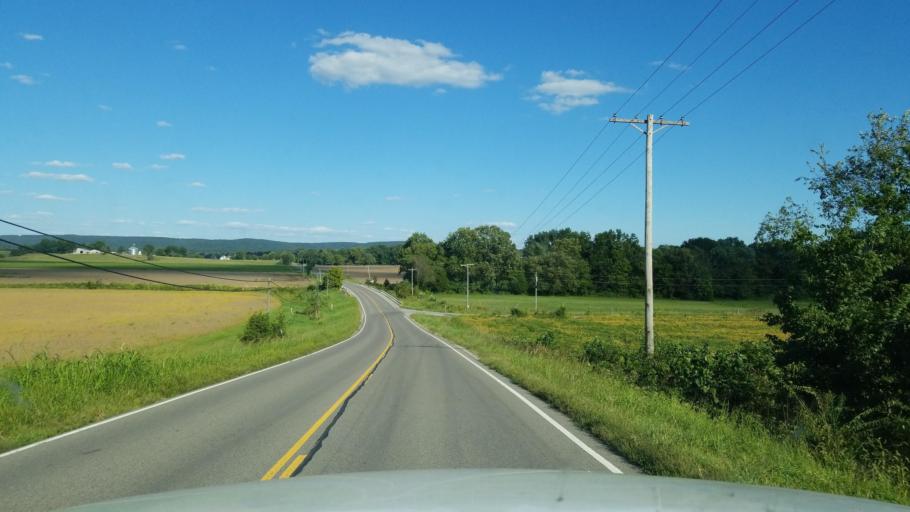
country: US
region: Illinois
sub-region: Saline County
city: Harrisburg
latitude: 37.6367
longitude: -88.5199
